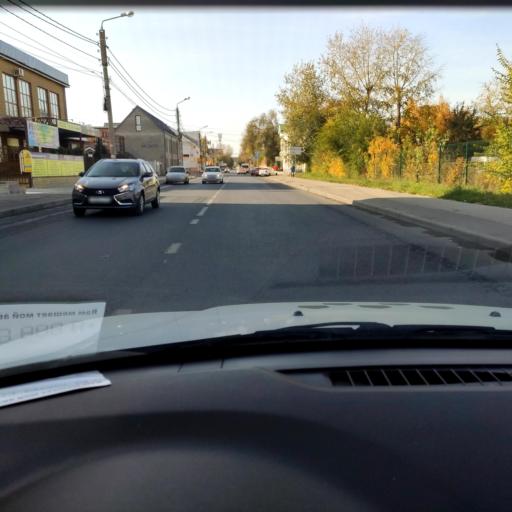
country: RU
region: Samara
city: Tol'yatti
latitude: 53.5171
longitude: 49.4099
